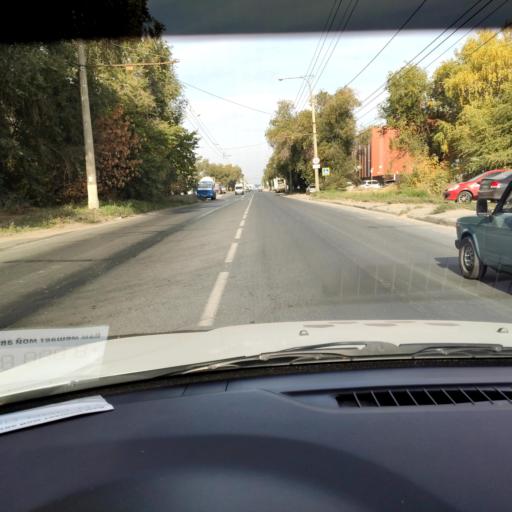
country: RU
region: Samara
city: Tol'yatti
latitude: 53.5663
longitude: 49.4571
